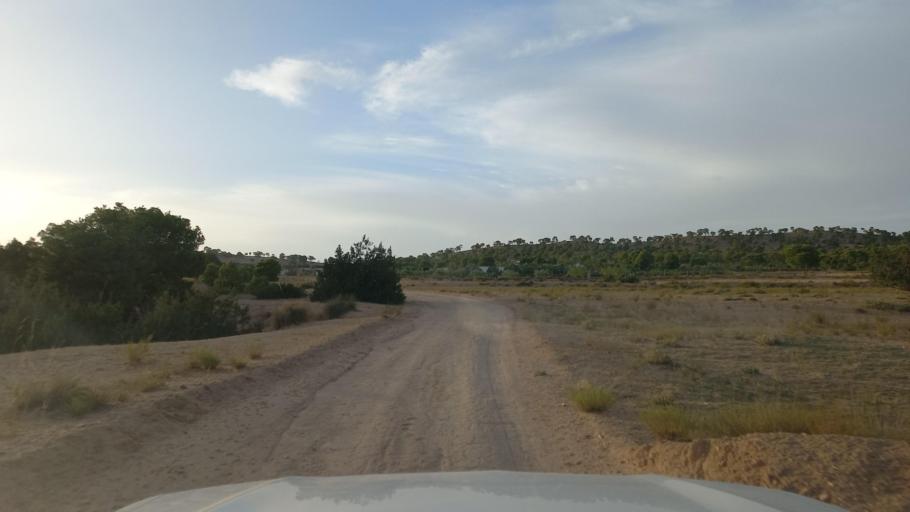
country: TN
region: Al Qasrayn
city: Sbiba
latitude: 35.4109
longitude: 8.9156
